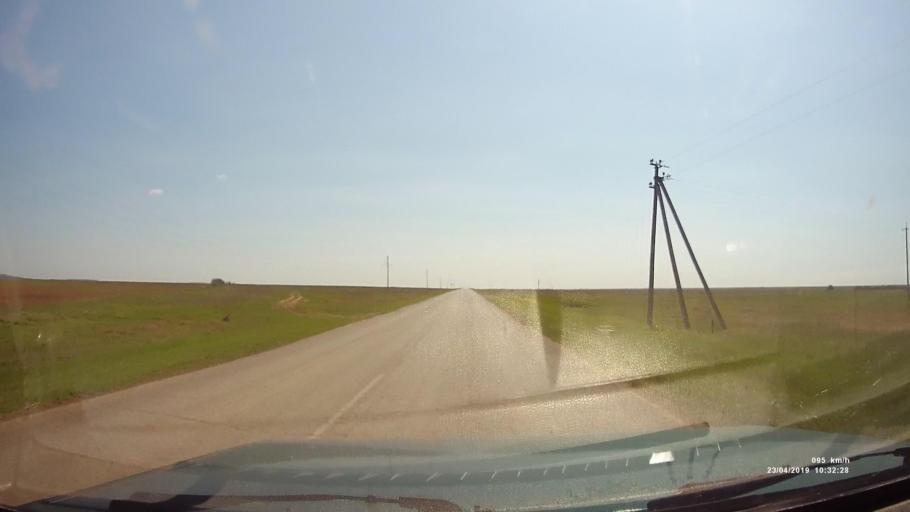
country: RU
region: Kalmykiya
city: Yashalta
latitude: 46.5800
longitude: 42.5787
